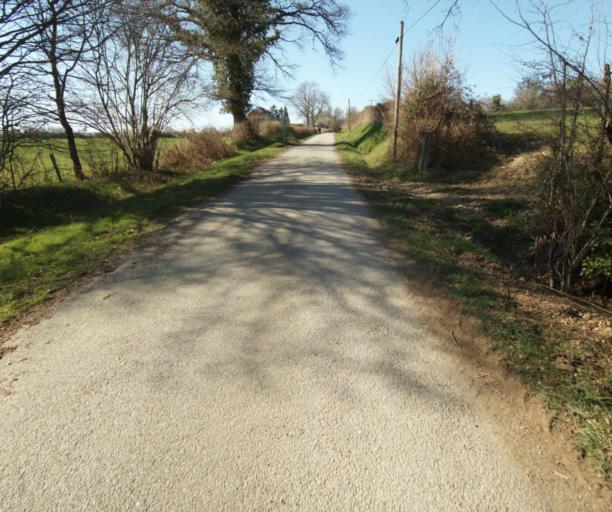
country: FR
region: Limousin
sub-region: Departement de la Correze
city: Chamboulive
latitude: 45.4779
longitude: 1.6908
